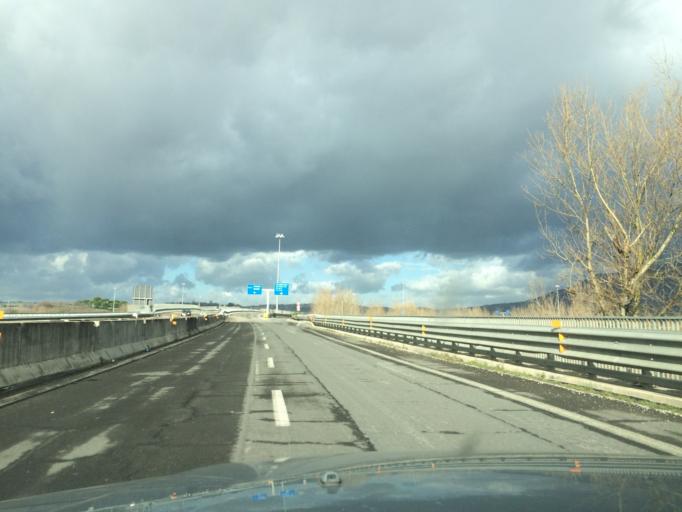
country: IT
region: Umbria
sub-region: Provincia di Terni
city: Terni
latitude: 42.5654
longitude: 12.5790
